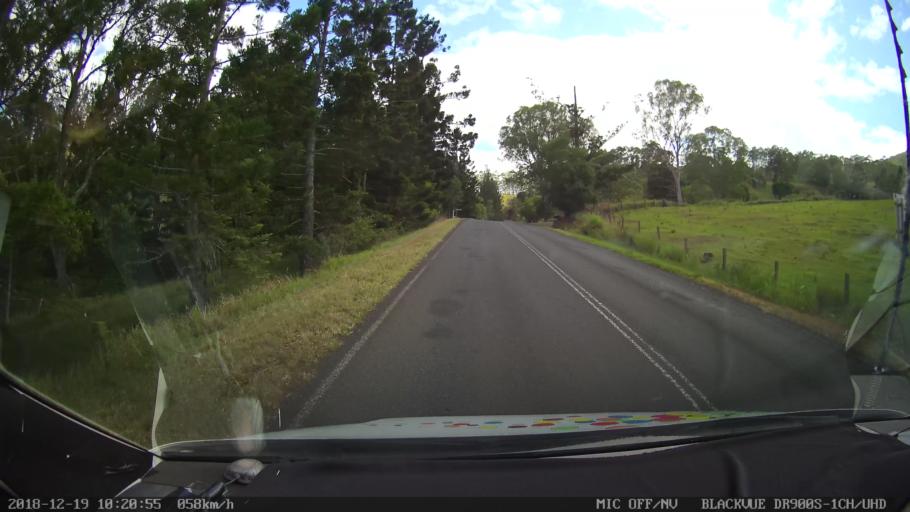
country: AU
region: New South Wales
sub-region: Kyogle
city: Kyogle
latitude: -28.6020
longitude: 153.0572
